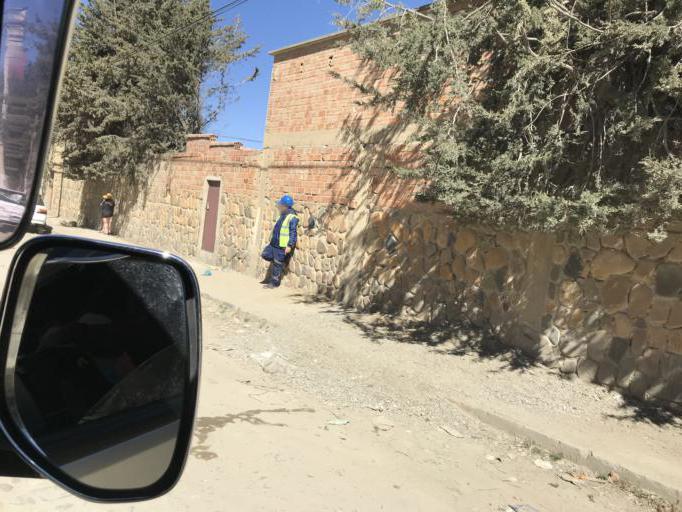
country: BO
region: La Paz
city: La Paz
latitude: -16.4882
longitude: -68.2111
